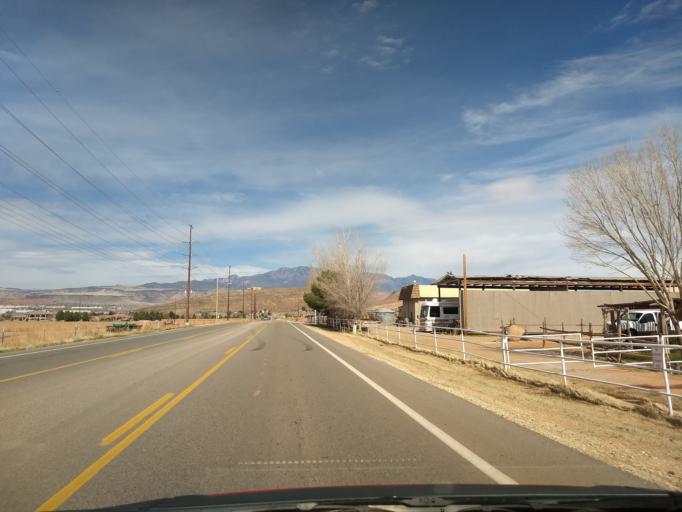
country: US
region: Utah
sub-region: Washington County
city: Washington
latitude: 37.0842
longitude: -113.4996
